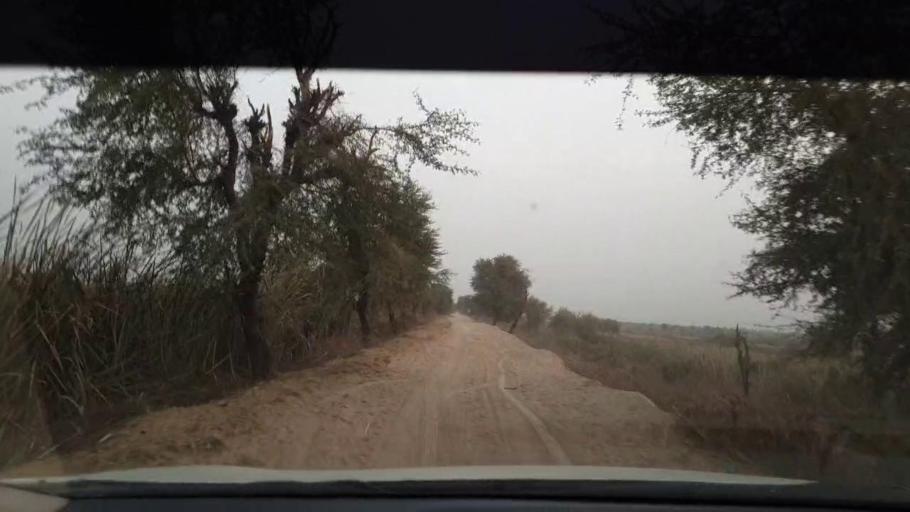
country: PK
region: Sindh
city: Berani
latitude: 25.8689
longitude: 68.7702
